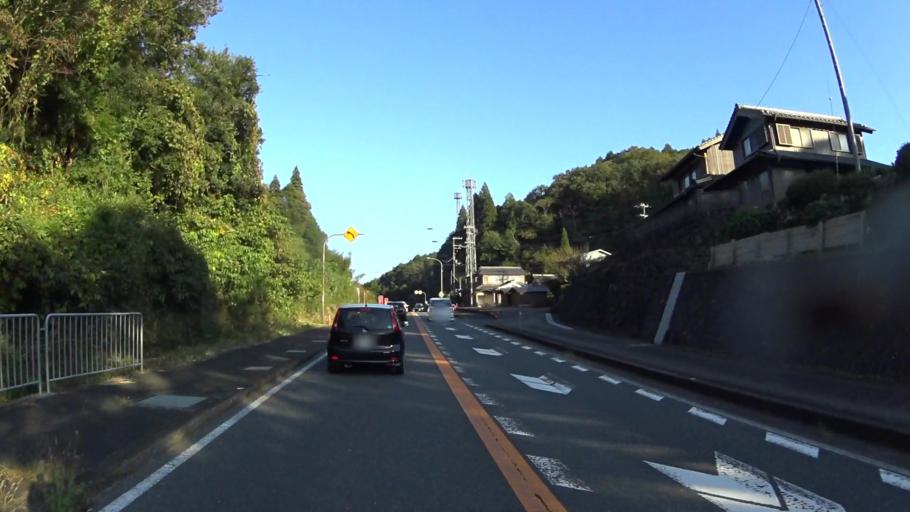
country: JP
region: Kyoto
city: Ayabe
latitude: 35.1879
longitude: 135.3188
